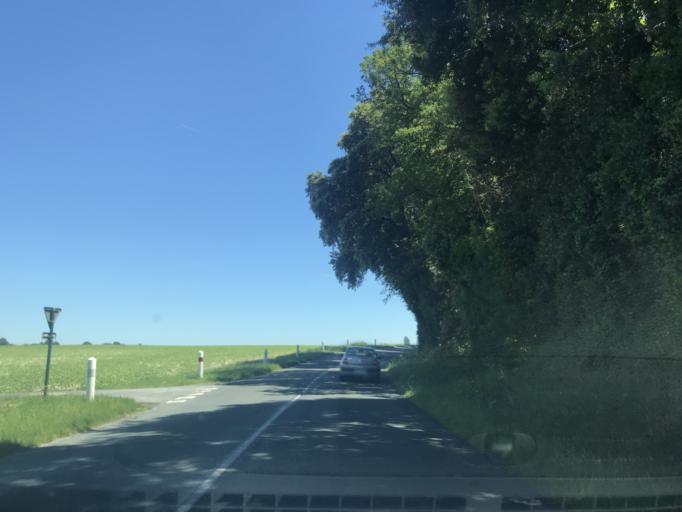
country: FR
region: Poitou-Charentes
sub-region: Departement de la Charente-Maritime
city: Meschers-sur-Gironde
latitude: 45.5923
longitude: -0.9662
